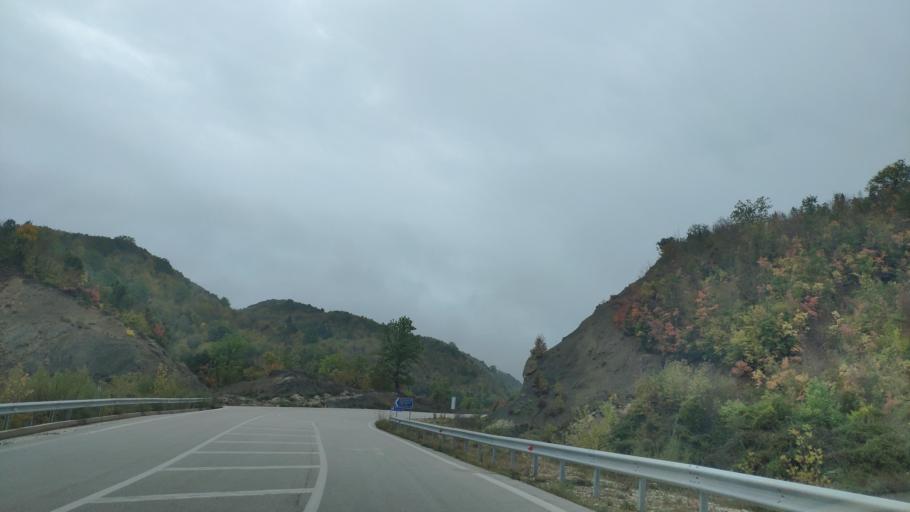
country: GR
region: Epirus
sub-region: Nomos Ioanninon
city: Pedini
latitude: 39.5177
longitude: 20.6898
